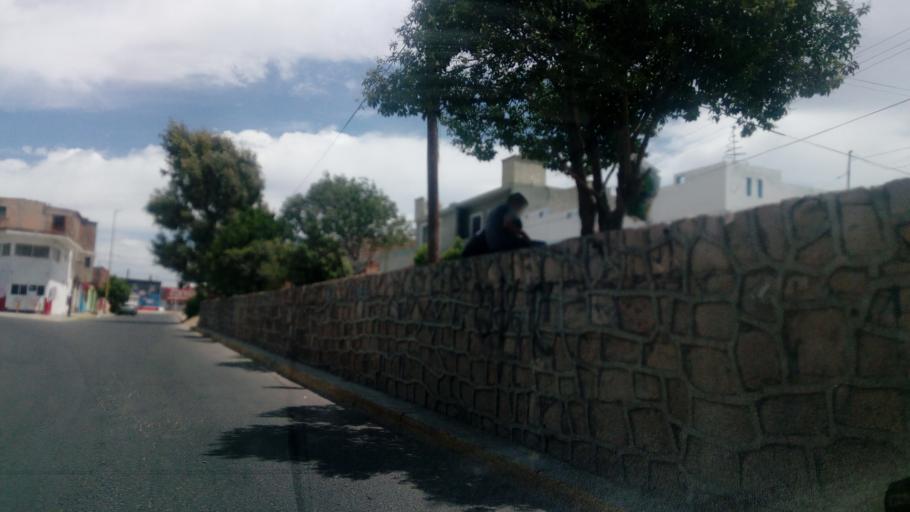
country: MX
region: Durango
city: Victoria de Durango
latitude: 24.0415
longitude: -104.6819
